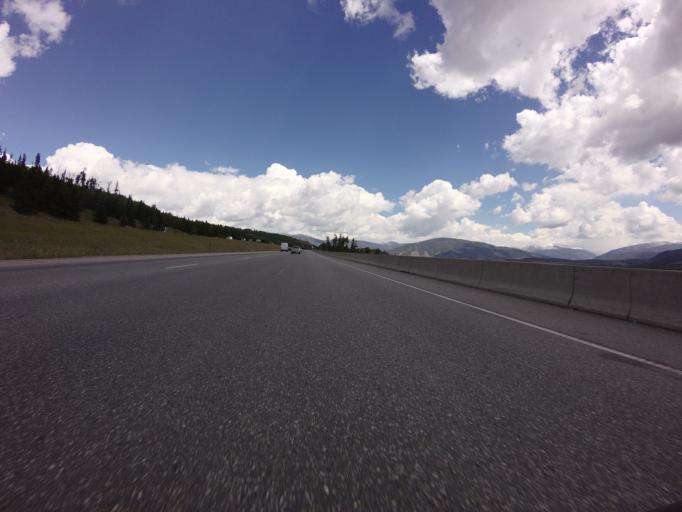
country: US
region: Colorado
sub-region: Summit County
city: Frisco
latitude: 39.5970
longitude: -106.0923
